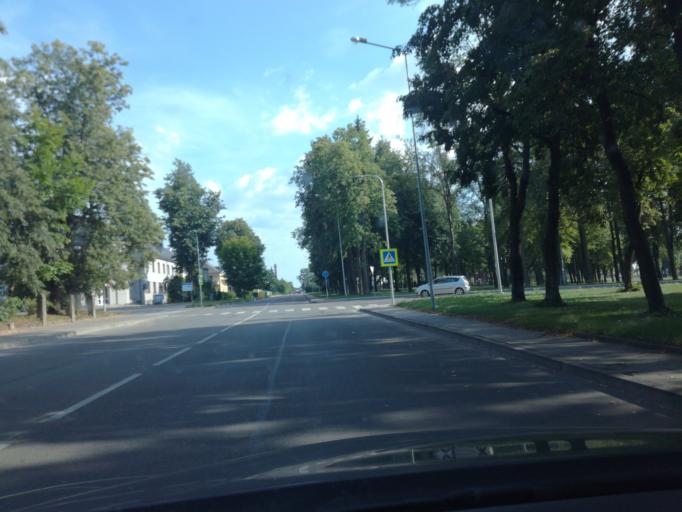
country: LT
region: Marijampoles apskritis
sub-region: Marijampole Municipality
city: Marijampole
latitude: 54.5457
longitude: 23.3478
